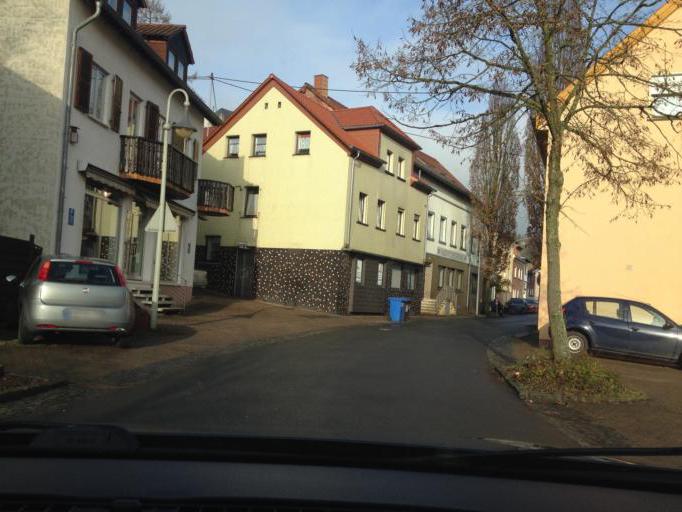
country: DE
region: Saarland
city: Marpingen
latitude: 49.4518
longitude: 7.0543
